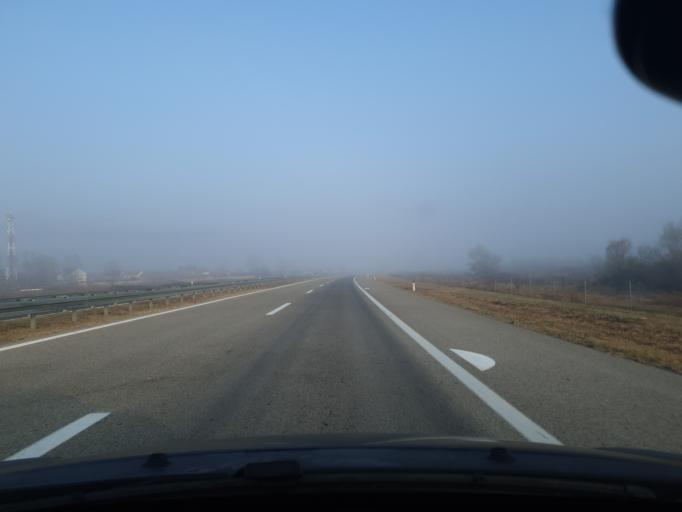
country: RS
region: Central Serbia
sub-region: Jablanicki Okrug
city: Leskovac
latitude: 42.9822
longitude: 22.0303
